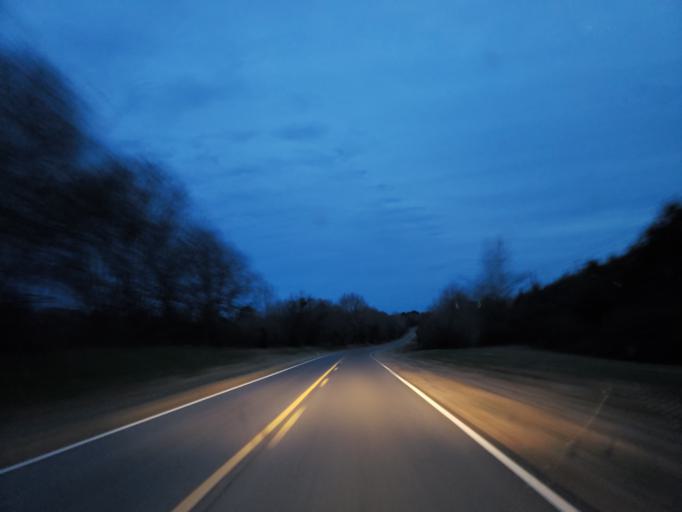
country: US
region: Alabama
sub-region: Greene County
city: Eutaw
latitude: 32.8970
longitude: -87.9604
